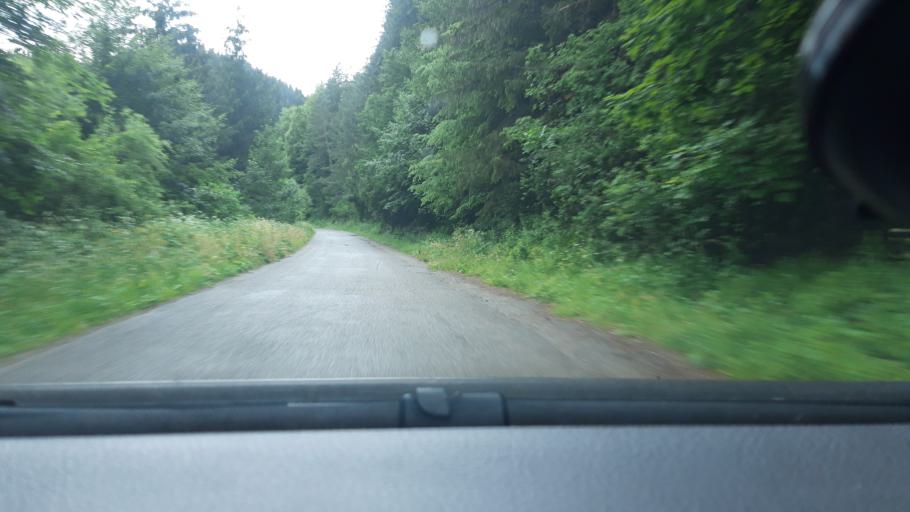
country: SK
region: Zilinsky
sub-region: Okres Martin
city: Martin
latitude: 49.0045
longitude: 18.9914
